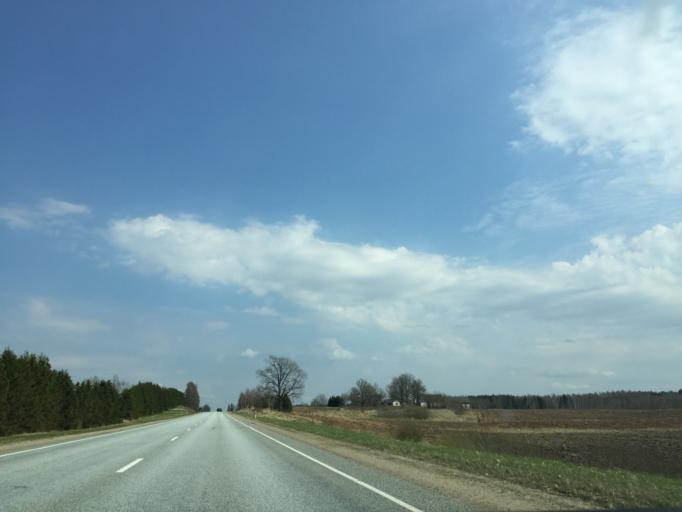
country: LV
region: Apes Novads
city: Ape
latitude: 57.5122
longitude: 26.6708
